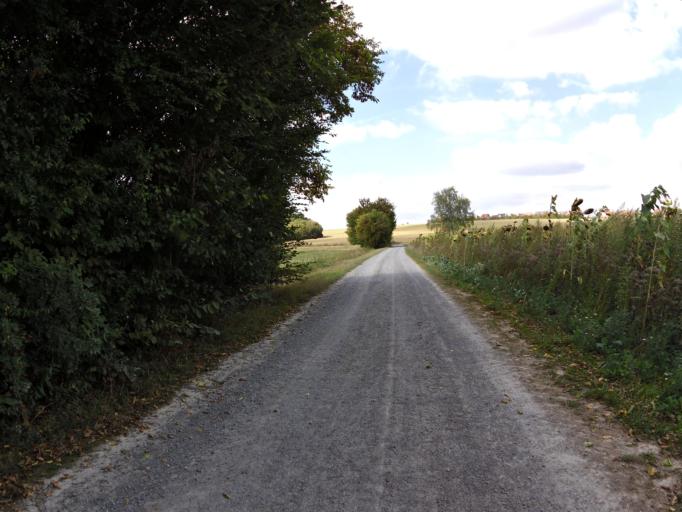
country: DE
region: Bavaria
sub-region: Regierungsbezirk Unterfranken
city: Hettstadt
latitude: 49.7945
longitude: 9.8128
